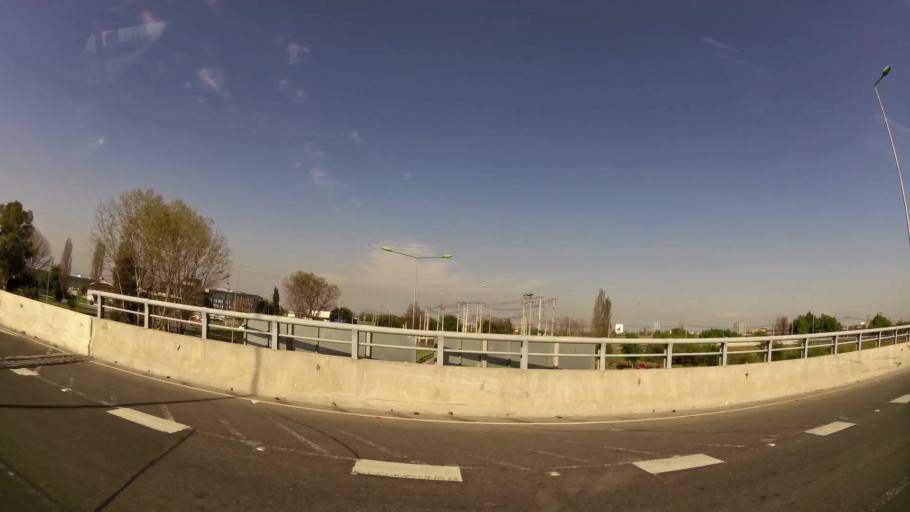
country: CL
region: Santiago Metropolitan
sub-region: Provincia de Santiago
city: Lo Prado
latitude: -33.4108
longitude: -70.7928
